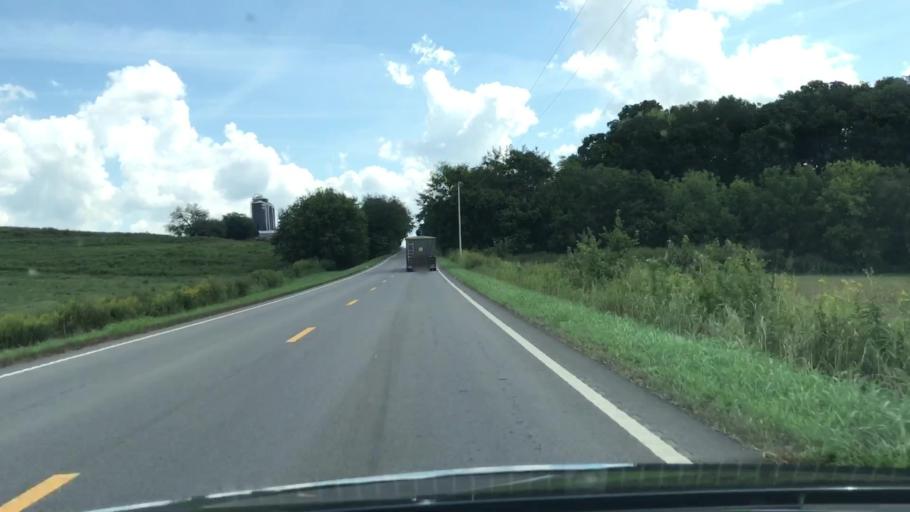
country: US
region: Tennessee
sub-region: Robertson County
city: Springfield
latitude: 36.6361
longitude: -86.9753
